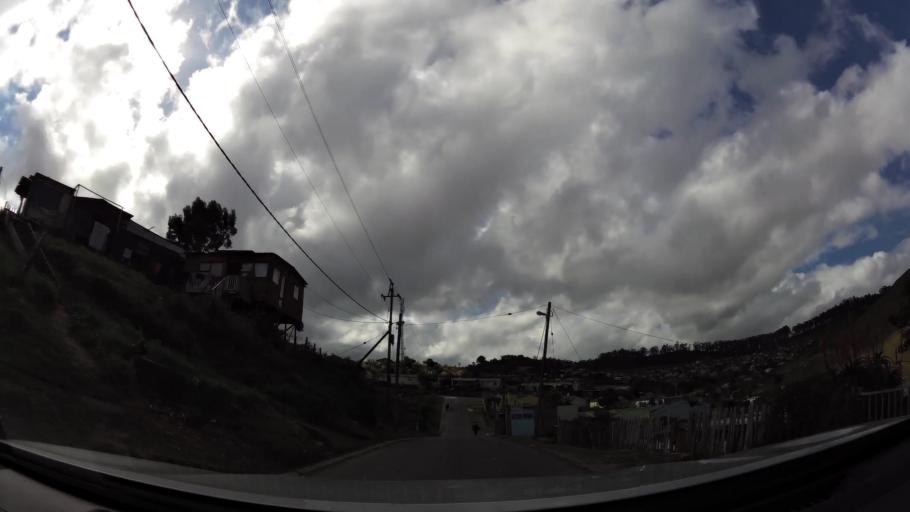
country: ZA
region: Western Cape
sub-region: Eden District Municipality
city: Knysna
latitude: -34.0543
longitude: 23.0954
